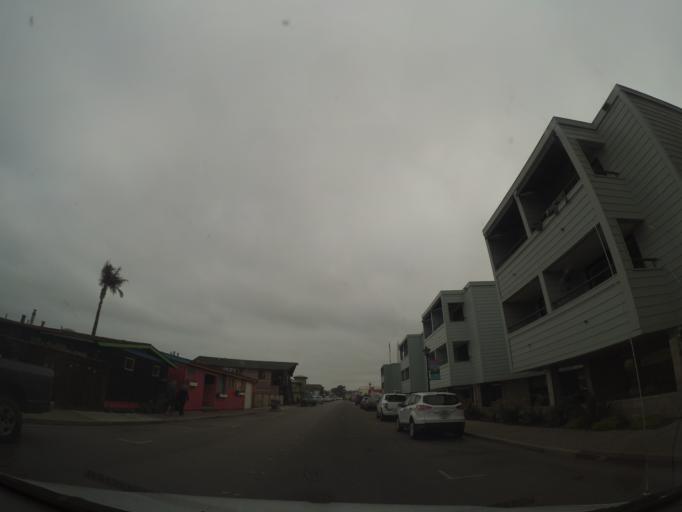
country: US
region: California
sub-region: San Luis Obispo County
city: Morro Bay
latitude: 35.3615
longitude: -120.8521
